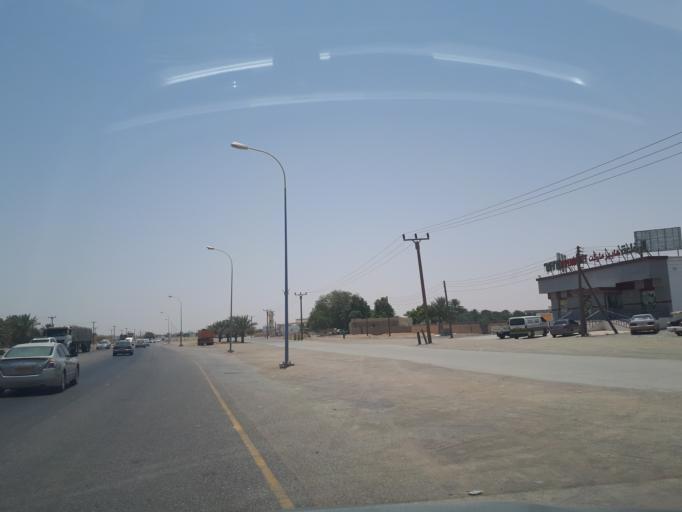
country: OM
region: Ash Sharqiyah
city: Badiyah
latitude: 22.5025
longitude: 58.7486
